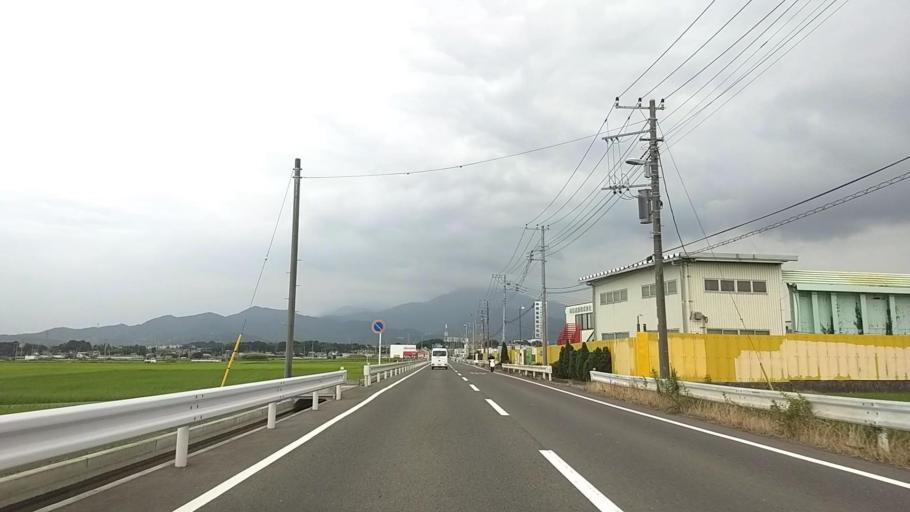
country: JP
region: Kanagawa
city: Isehara
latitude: 35.3837
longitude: 139.3372
